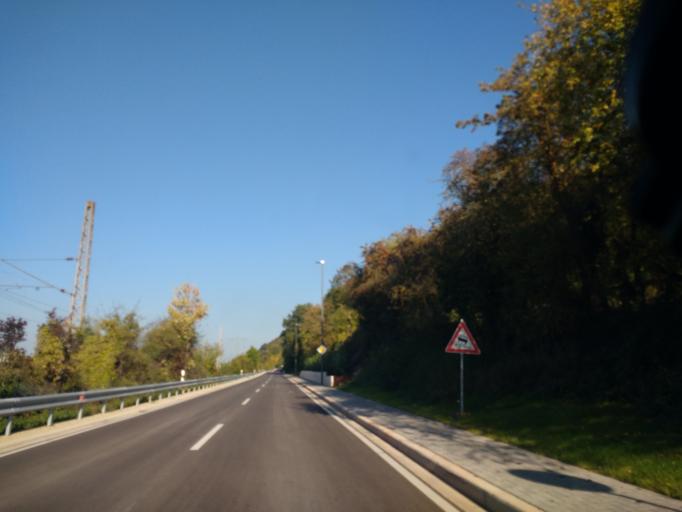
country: DE
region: Rheinland-Pfalz
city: Konz
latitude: 49.7065
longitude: 6.5895
